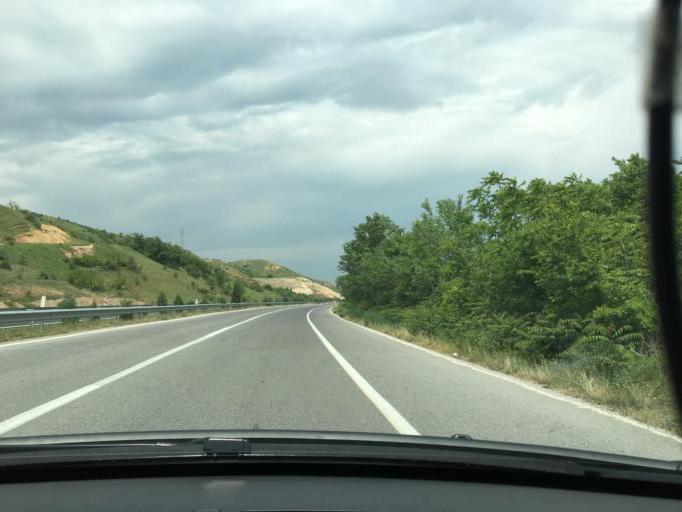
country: MK
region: Demir Kapija
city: Demir Kapija
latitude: 41.4285
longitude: 22.1845
